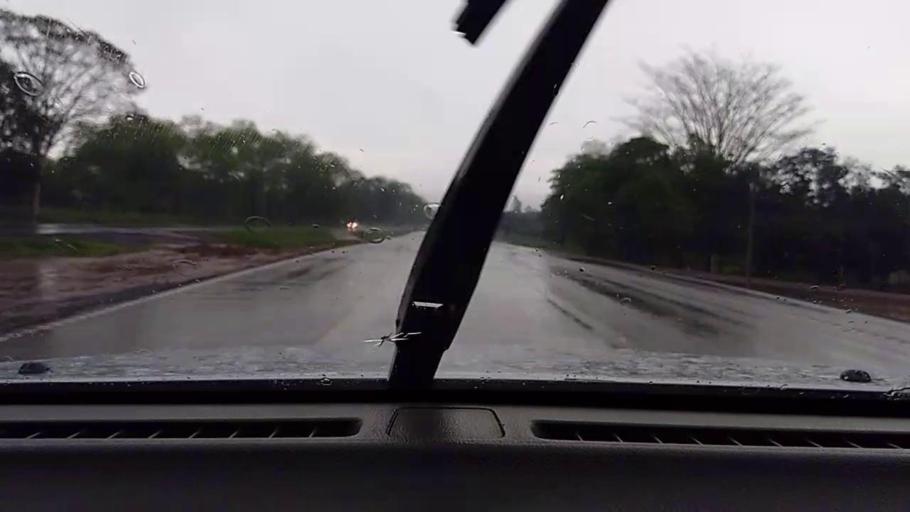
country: PY
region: Caaguazu
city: Repatriacion
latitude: -25.4544
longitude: -55.9110
